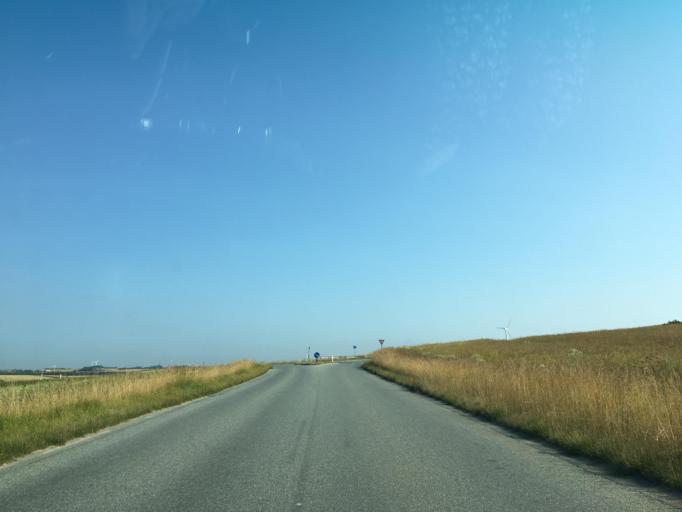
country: DK
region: North Denmark
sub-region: Thisted Kommune
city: Hurup
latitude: 56.7577
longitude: 8.4388
